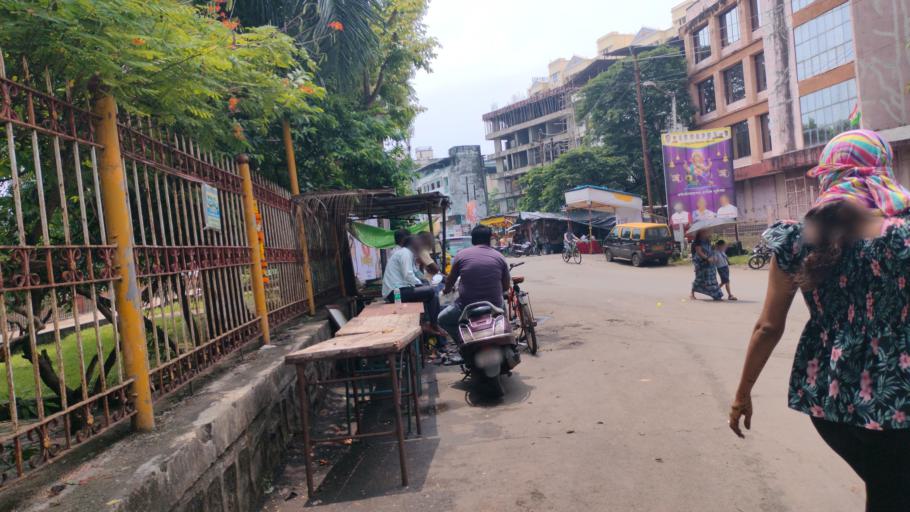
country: IN
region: Maharashtra
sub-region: Thane
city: Virar
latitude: 19.4105
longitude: 72.8281
